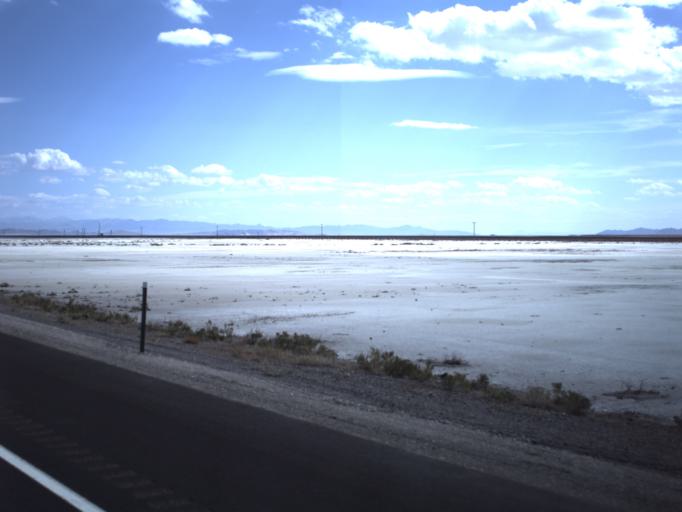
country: US
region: Utah
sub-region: Tooele County
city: Wendover
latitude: 40.7311
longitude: -113.5104
